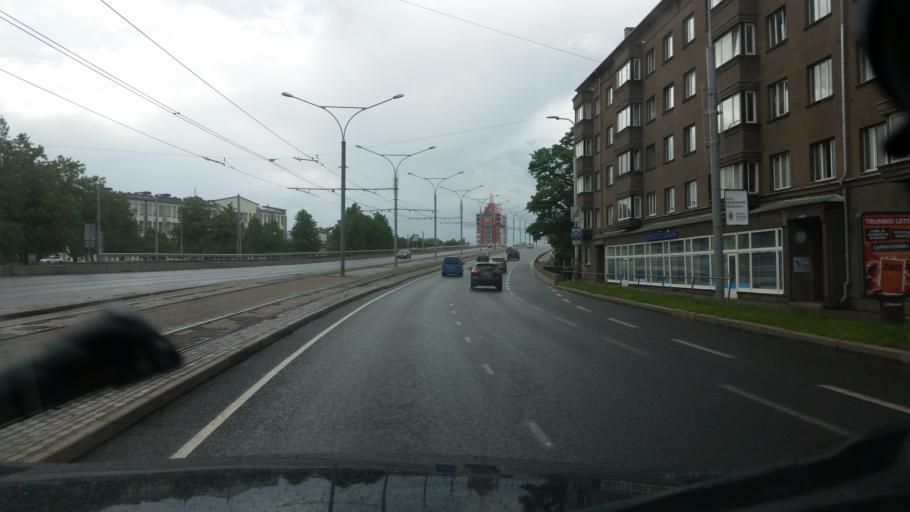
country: EE
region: Harju
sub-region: Tallinna linn
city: Tallinn
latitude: 59.4222
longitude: 24.7425
